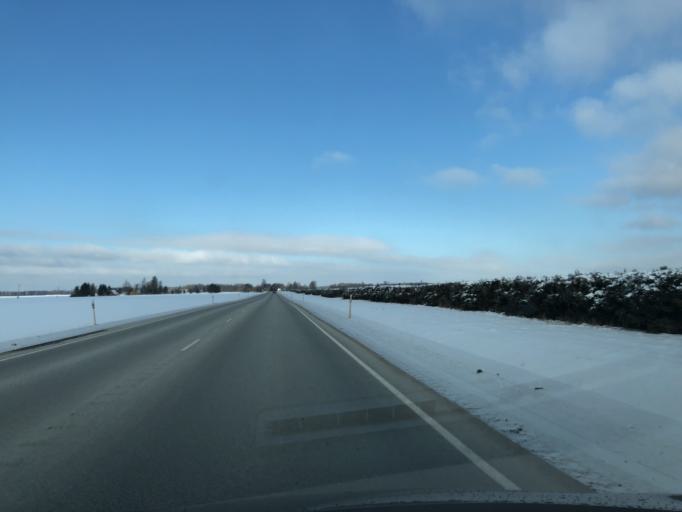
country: EE
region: Jaervamaa
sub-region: Paide linn
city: Paide
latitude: 58.7789
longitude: 25.7606
